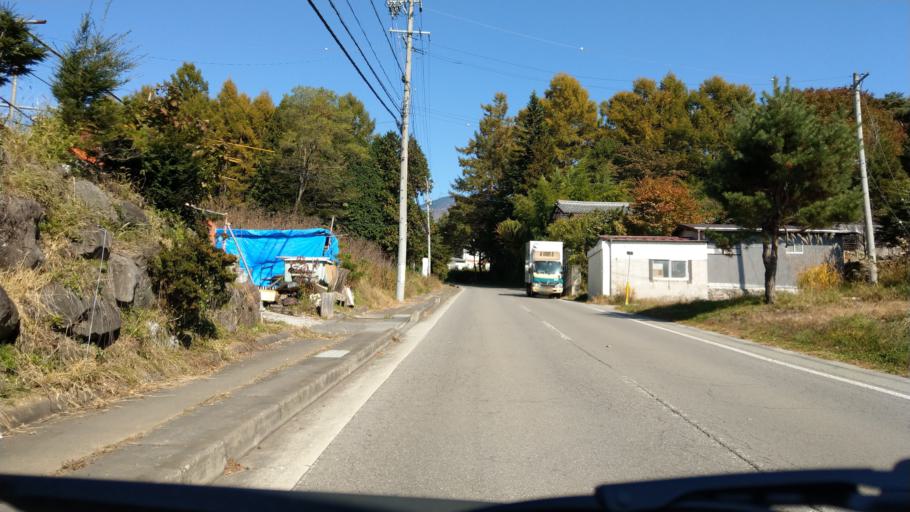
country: JP
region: Nagano
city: Komoro
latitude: 36.3470
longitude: 138.4446
